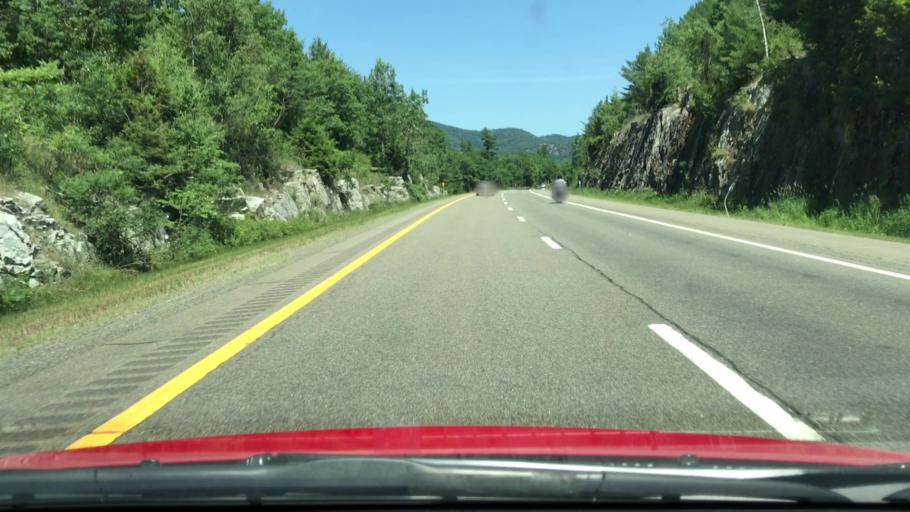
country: US
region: New York
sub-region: Essex County
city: Elizabethtown
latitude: 44.3505
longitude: -73.5333
